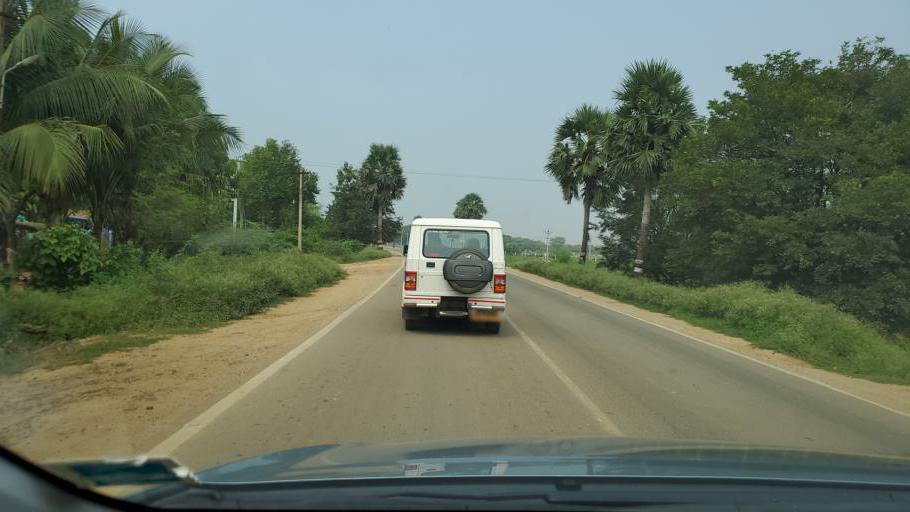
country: IN
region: Tamil Nadu
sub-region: Ariyalur
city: Ariyalur
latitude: 11.1229
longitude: 79.1438
